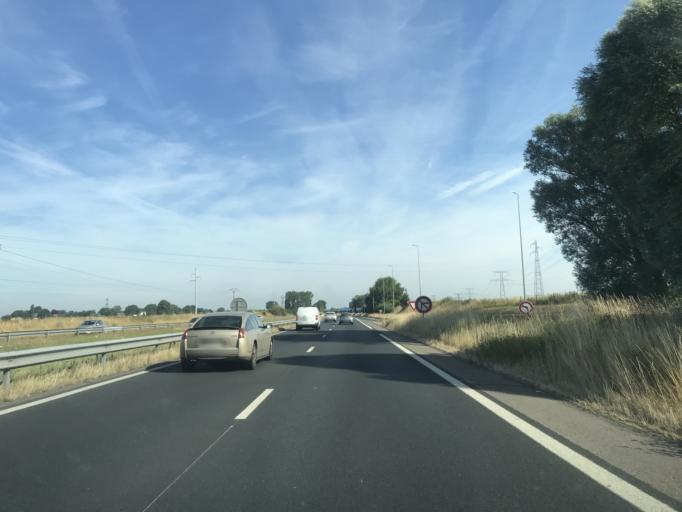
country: FR
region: Haute-Normandie
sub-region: Departement de la Seine-Maritime
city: La Vaupaliere
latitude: 49.4966
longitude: 0.9963
